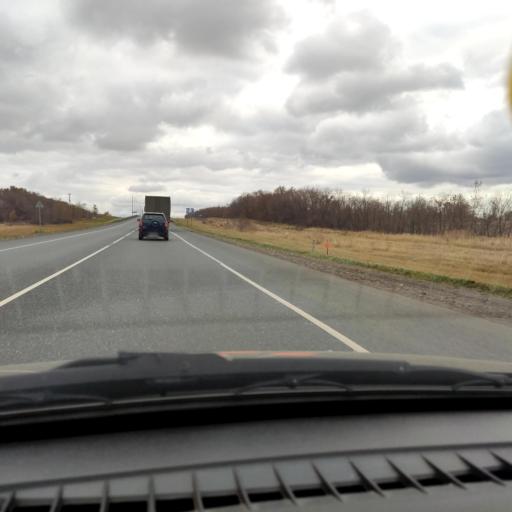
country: RU
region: Samara
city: Mezhdurechensk
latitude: 53.2453
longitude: 48.9960
